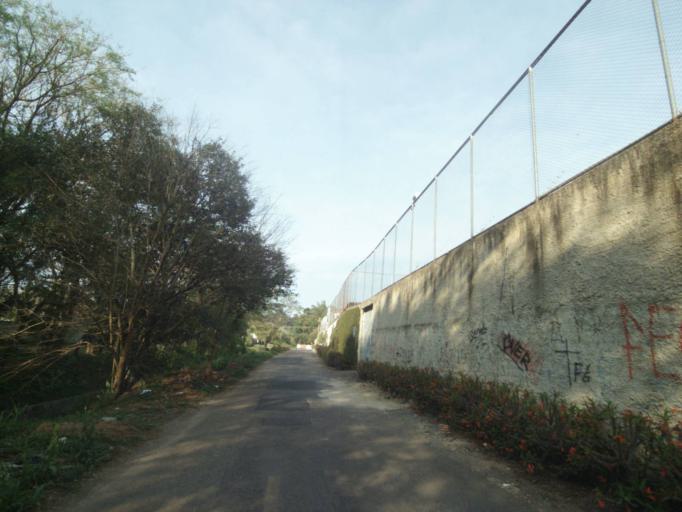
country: BR
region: Parana
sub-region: Curitiba
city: Curitiba
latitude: -25.4545
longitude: -49.3124
